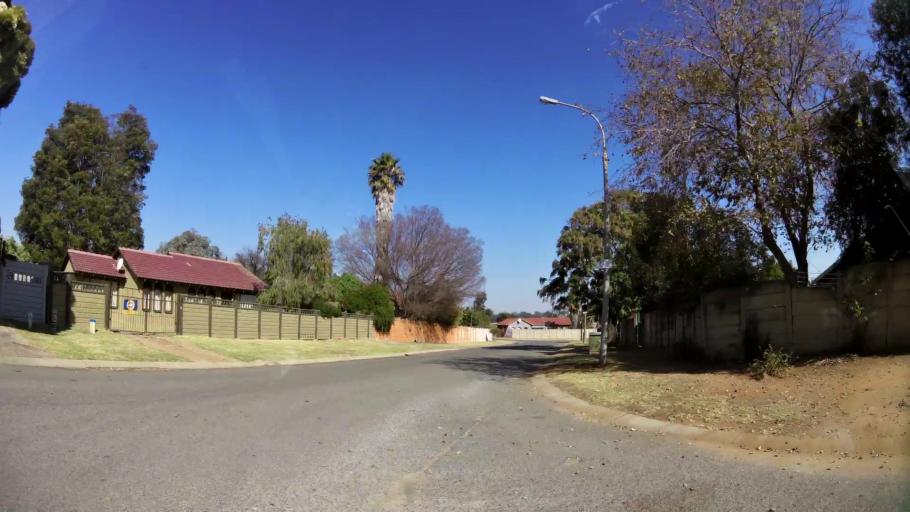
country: ZA
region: Gauteng
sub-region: City of Johannesburg Metropolitan Municipality
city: Modderfontein
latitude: -26.0515
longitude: 28.2016
